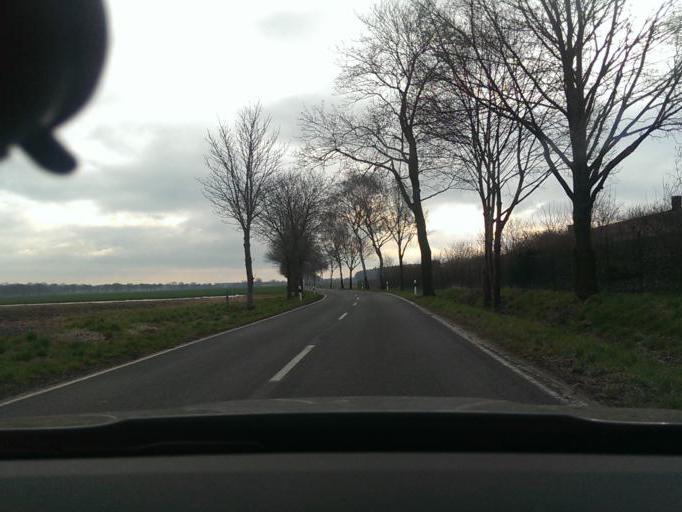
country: DE
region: Lower Saxony
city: Lindwedel
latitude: 52.5799
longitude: 9.6634
